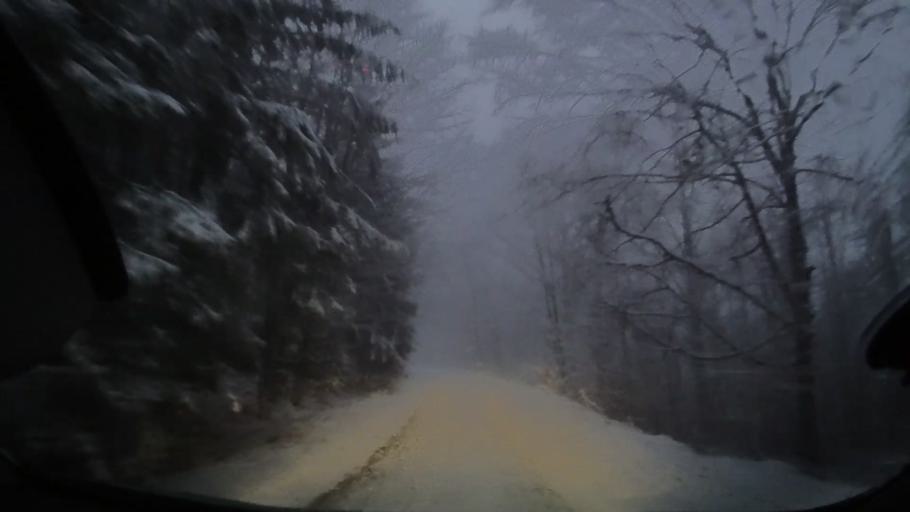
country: RO
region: Alba
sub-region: Comuna Avram Iancu
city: Avram Iancu
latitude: 46.3102
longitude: 22.8133
